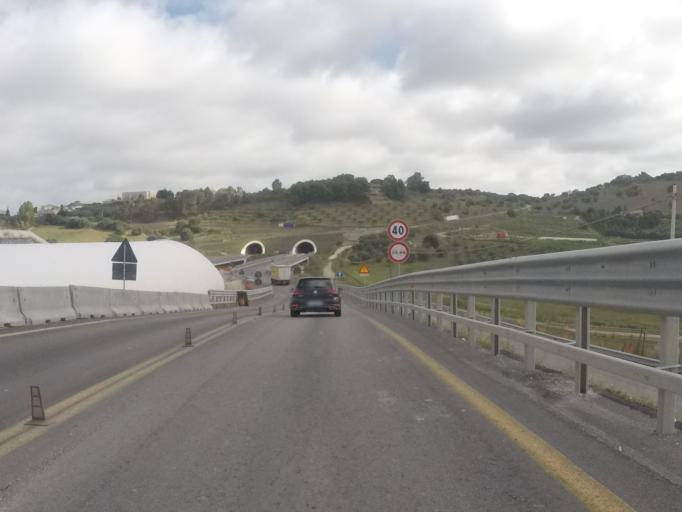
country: IT
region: Sicily
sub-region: Provincia di Caltanissetta
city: San Cataldo
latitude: 37.4569
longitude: 13.9929
